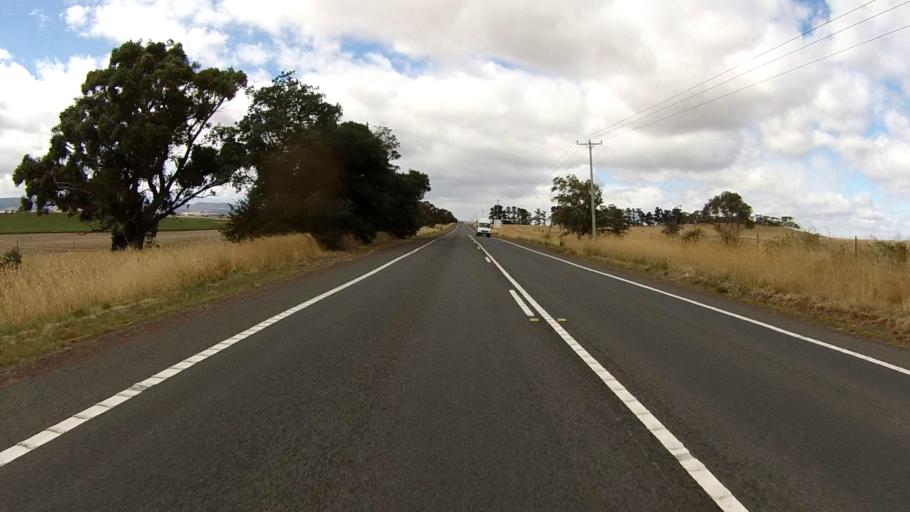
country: AU
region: Tasmania
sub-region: Northern Midlands
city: Evandale
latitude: -41.9063
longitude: 147.4791
